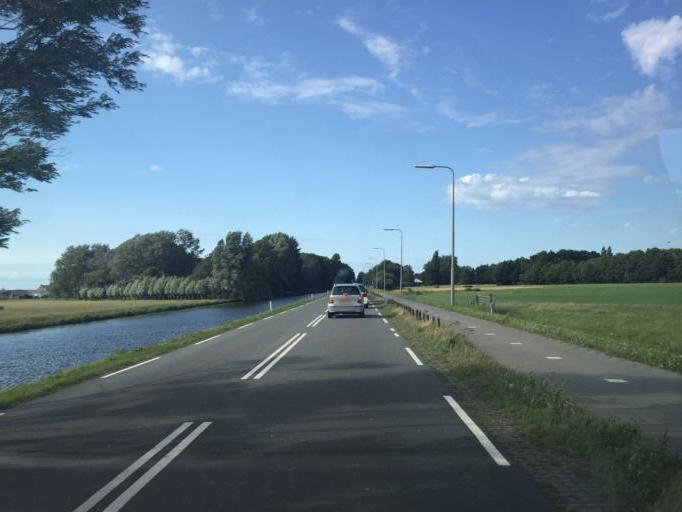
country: NL
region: South Holland
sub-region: Gemeente Teylingen
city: Voorhout
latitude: 52.2125
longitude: 4.4795
